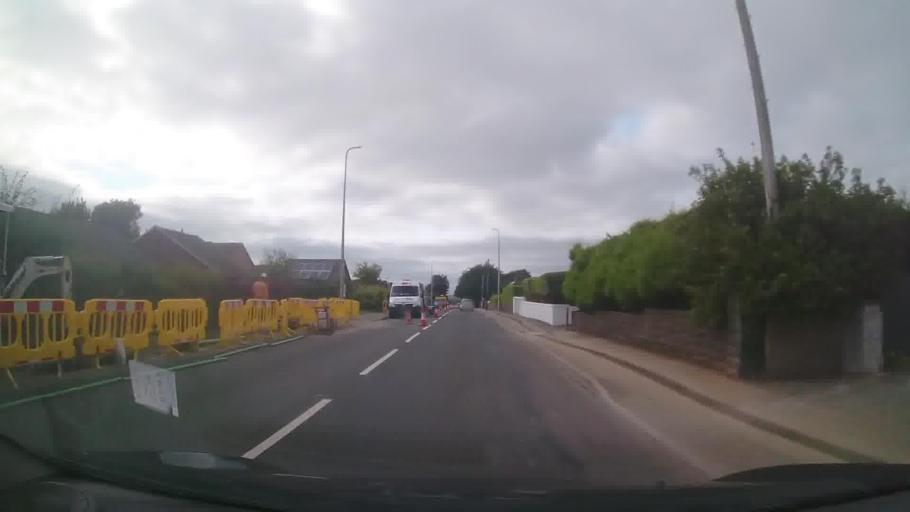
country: GB
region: Wales
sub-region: Pembrokeshire
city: Steynton
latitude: 51.7298
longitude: -5.0126
